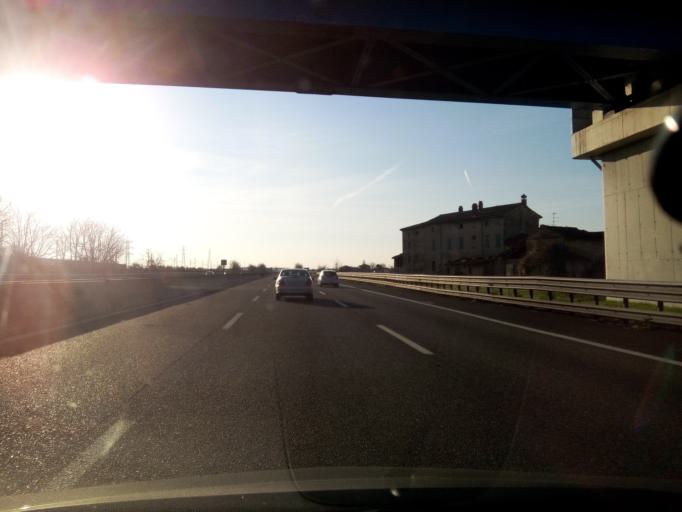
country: IT
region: Emilia-Romagna
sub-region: Provincia di Piacenza
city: Roveleto
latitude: 44.9840
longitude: 9.8552
